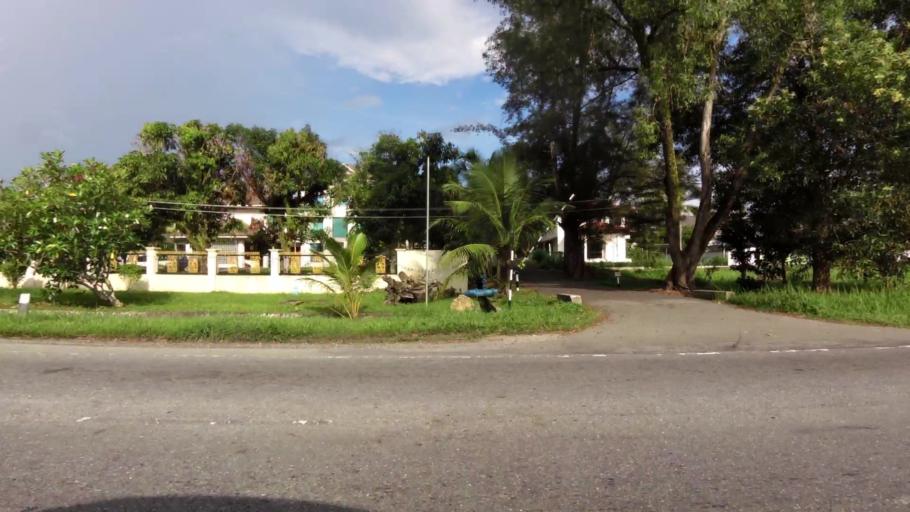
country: BN
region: Brunei and Muara
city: Bandar Seri Begawan
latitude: 4.9669
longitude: 114.9767
